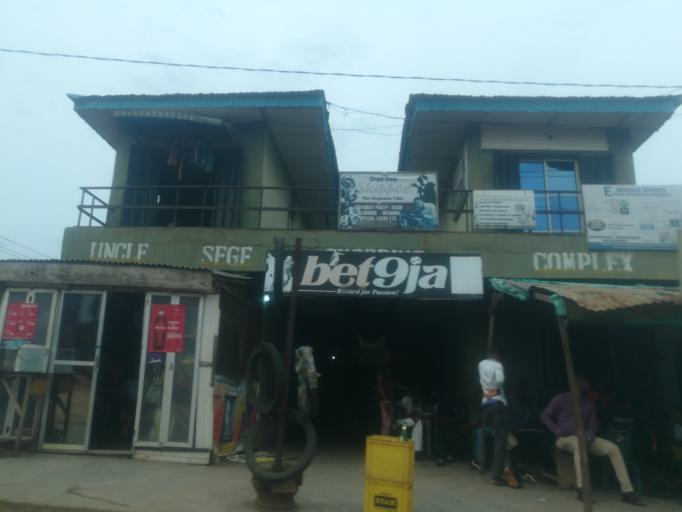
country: NG
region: Oyo
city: Egbeda
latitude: 7.3846
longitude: 3.9940
